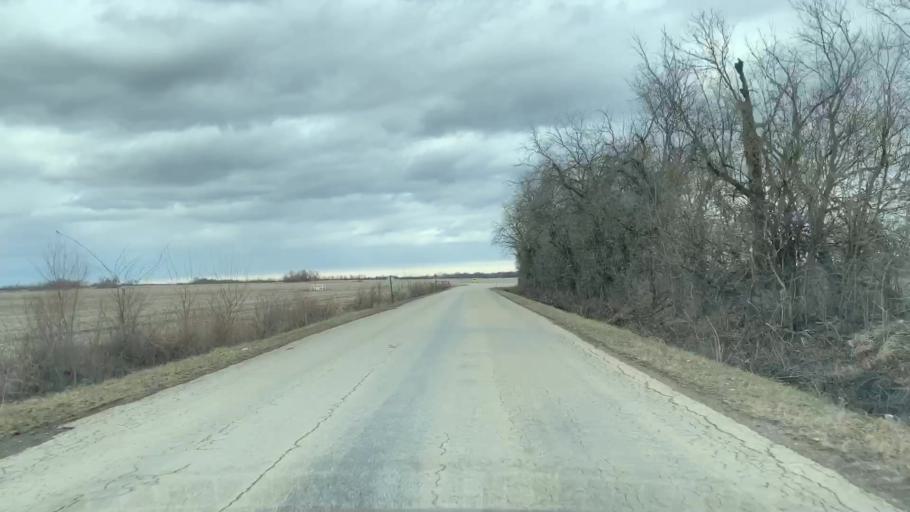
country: US
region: Kansas
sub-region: Allen County
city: Humboldt
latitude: 37.8113
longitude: -95.4705
